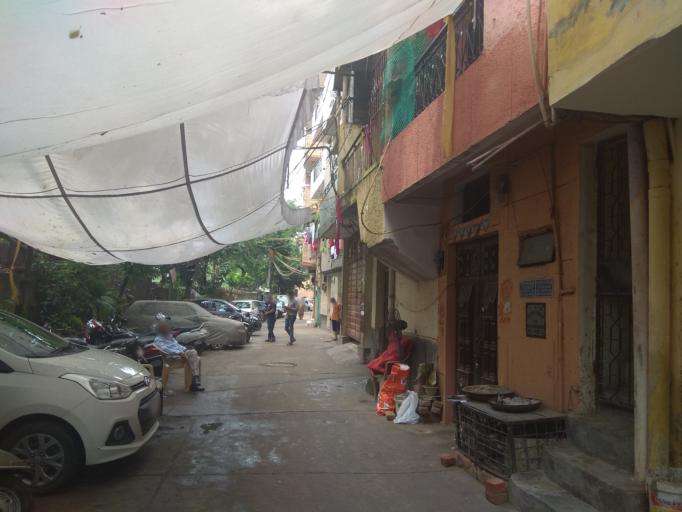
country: IN
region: NCT
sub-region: New Delhi
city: New Delhi
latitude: 28.5747
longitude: 77.2551
